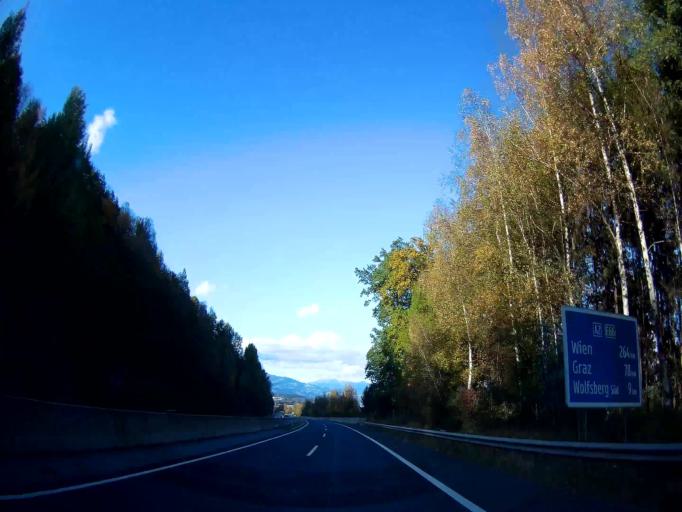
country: AT
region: Carinthia
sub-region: Politischer Bezirk Wolfsberg
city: Sankt Andrae
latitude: 46.7543
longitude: 14.8164
